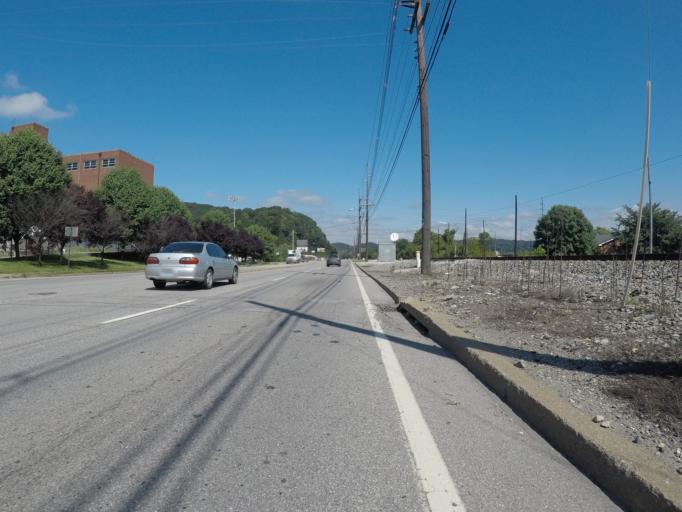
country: US
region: Kentucky
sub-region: Boyd County
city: Ashland
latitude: 38.4530
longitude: -82.6124
